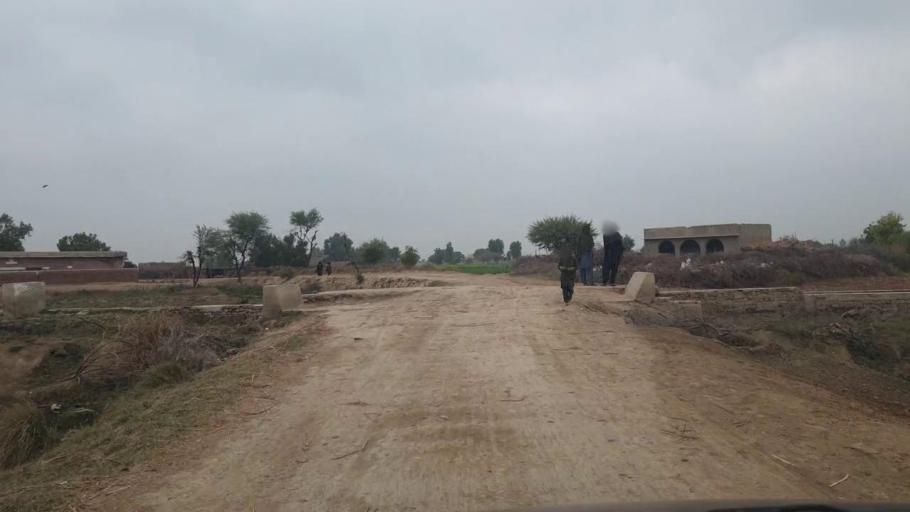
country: PK
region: Sindh
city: Shahdadpur
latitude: 25.9010
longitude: 68.6951
